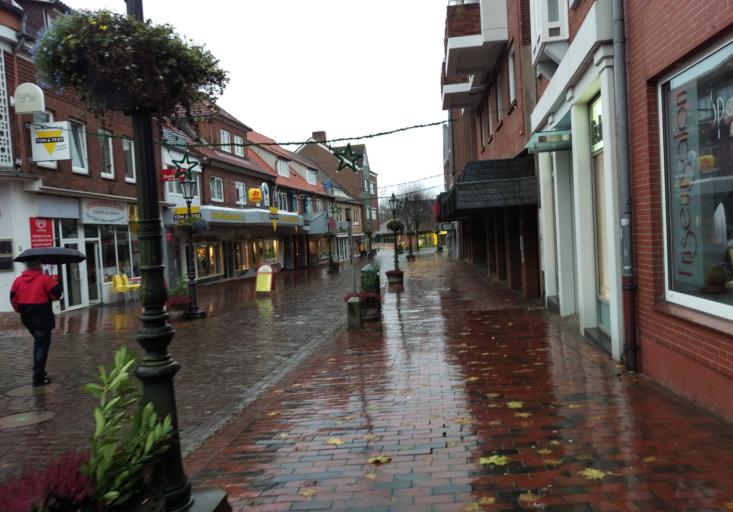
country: DE
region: Schleswig-Holstein
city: Oldenburg in Holstein
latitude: 54.2917
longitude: 10.8885
